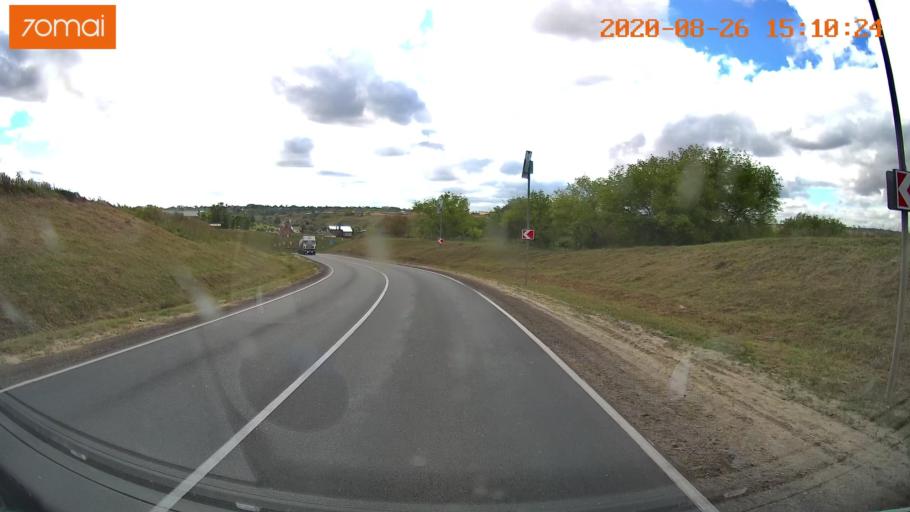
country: RU
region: Rjazan
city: Oktyabr'skiy
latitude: 54.1567
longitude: 38.6832
